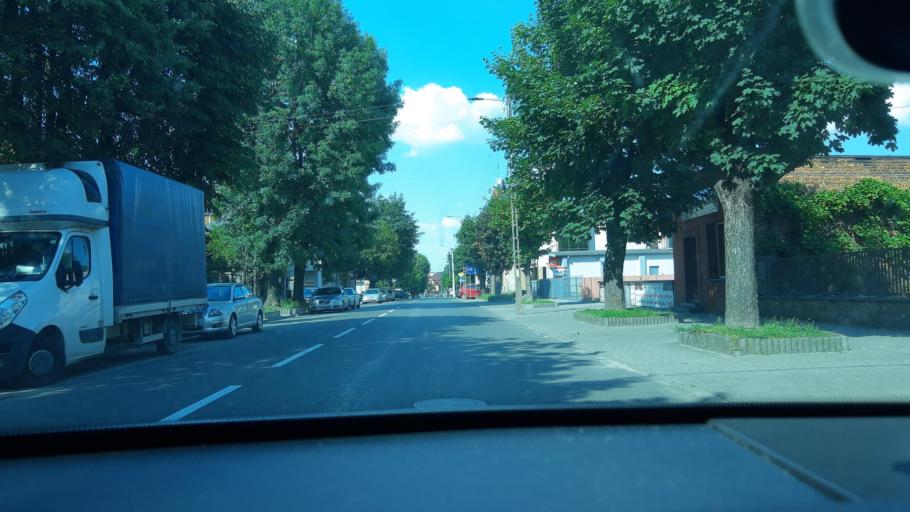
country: PL
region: Lodz Voivodeship
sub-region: Powiat zdunskowolski
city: Zdunska Wola
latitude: 51.6031
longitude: 18.9388
